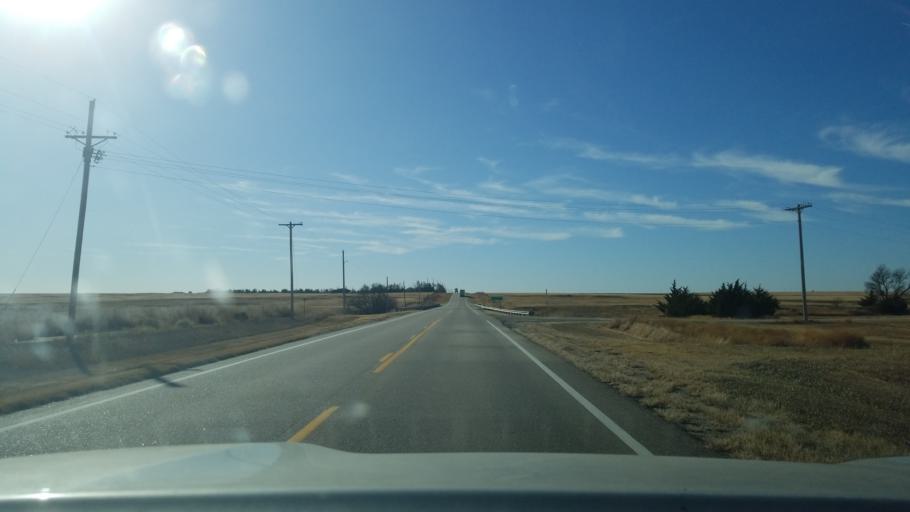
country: US
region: Kansas
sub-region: Ness County
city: Ness City
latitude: 38.4084
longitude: -99.8985
